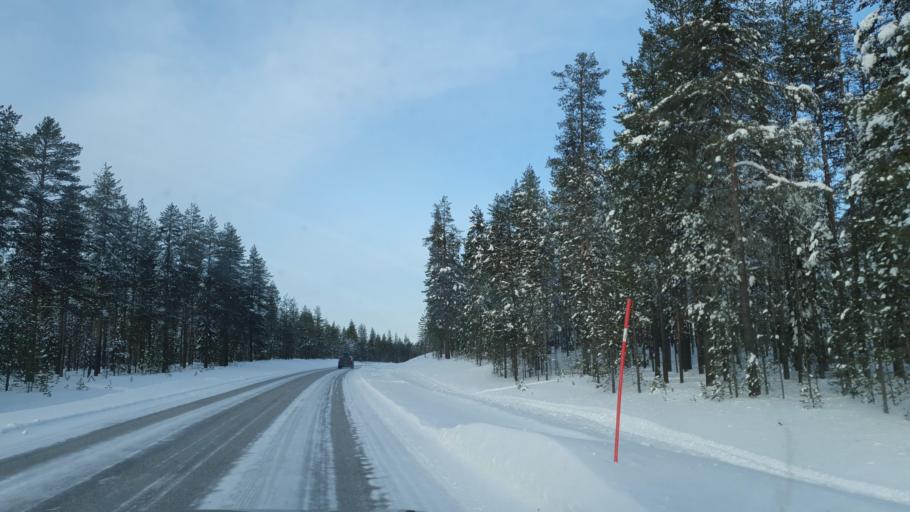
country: FI
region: Lapland
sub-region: Tunturi-Lappi
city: Kolari
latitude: 67.4534
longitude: 23.8451
